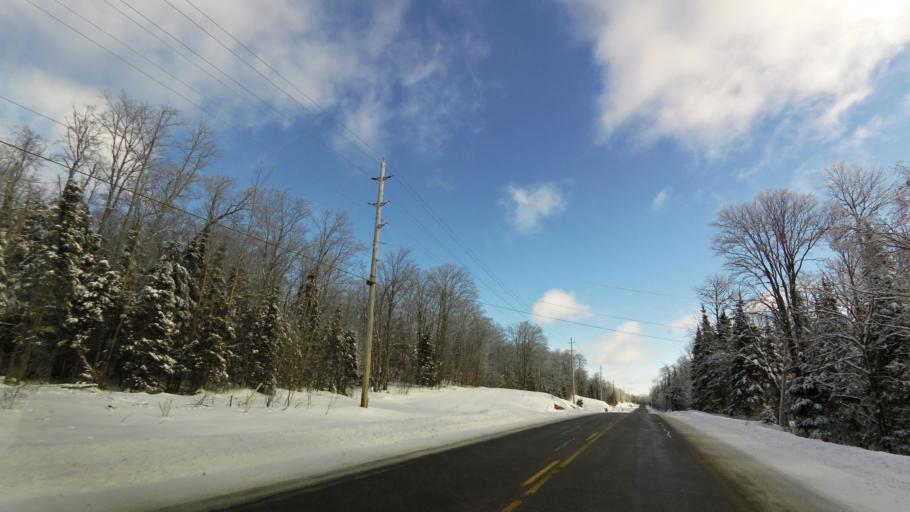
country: CA
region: Ontario
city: Bancroft
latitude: 45.0119
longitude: -78.3287
